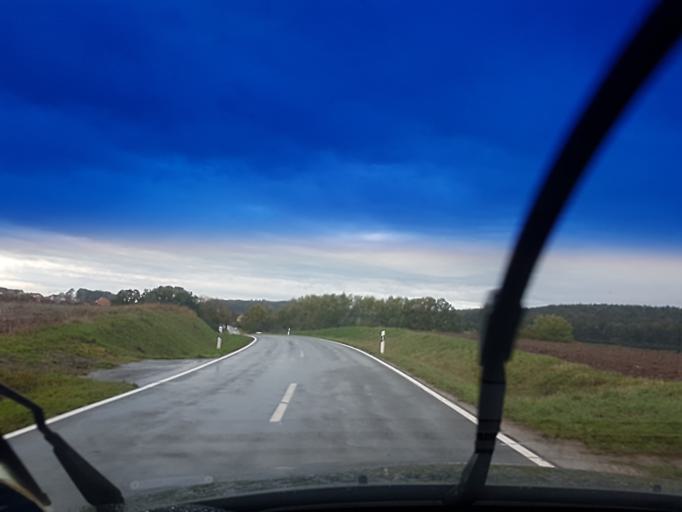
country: DE
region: Bavaria
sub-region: Upper Franconia
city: Schlusselfeld
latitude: 49.7627
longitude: 10.6643
